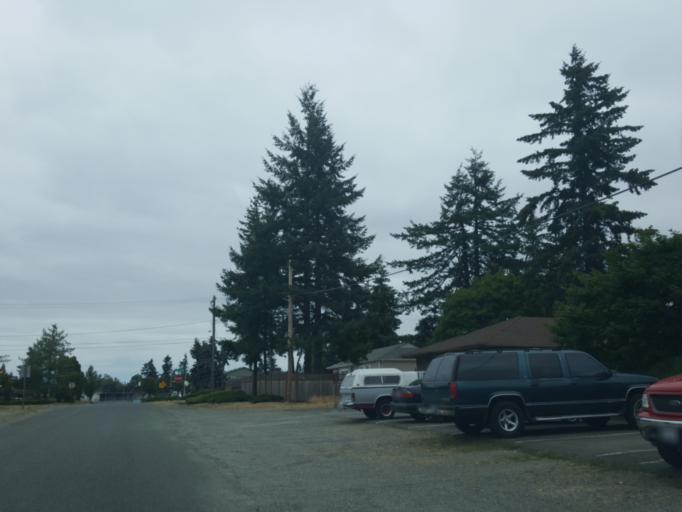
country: US
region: Washington
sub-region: Pierce County
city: Lakewood
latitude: 47.1585
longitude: -122.4982
